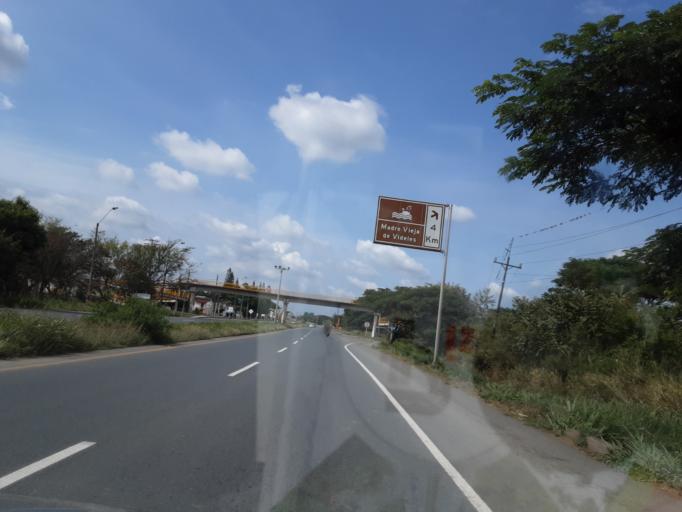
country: CO
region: Valle del Cauca
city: Guacari
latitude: 3.7690
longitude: -76.3272
